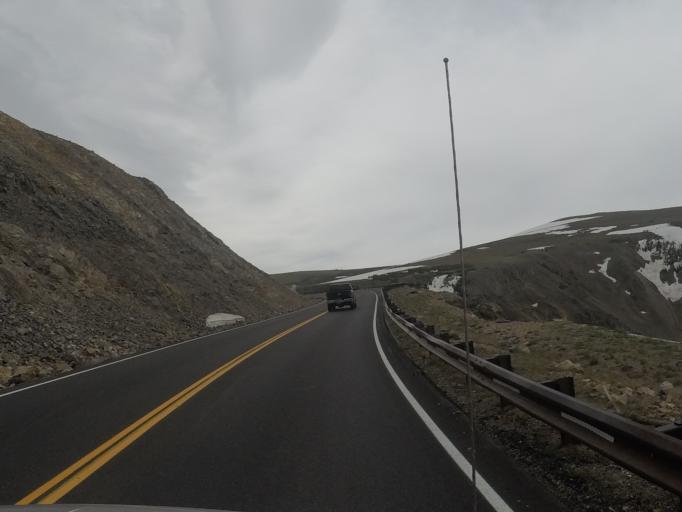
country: US
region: Montana
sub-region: Carbon County
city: Red Lodge
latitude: 45.0322
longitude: -109.4120
